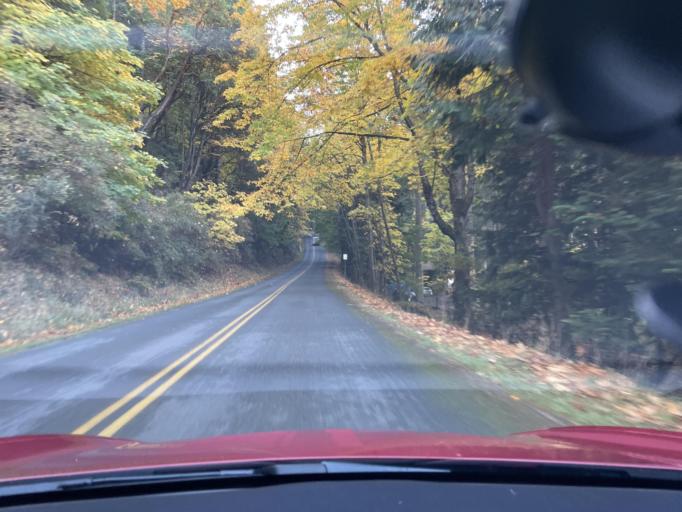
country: US
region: Washington
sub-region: San Juan County
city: Friday Harbor
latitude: 48.5413
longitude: -123.1585
